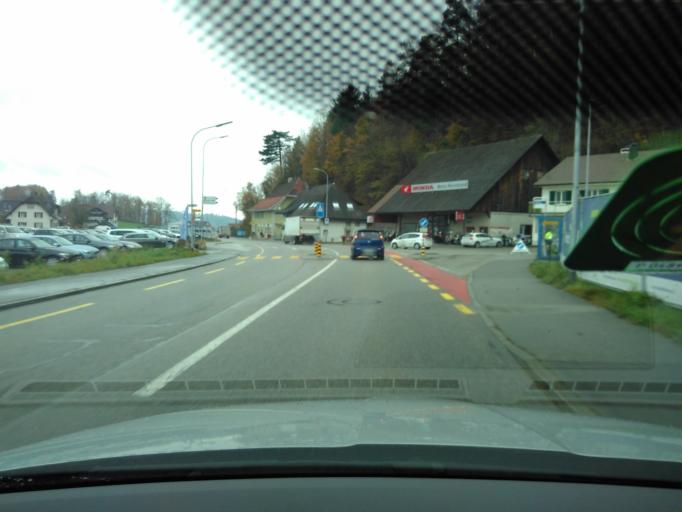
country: CH
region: Aargau
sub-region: Bezirk Zofingen
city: Kirchleerau
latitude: 47.2760
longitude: 8.0632
